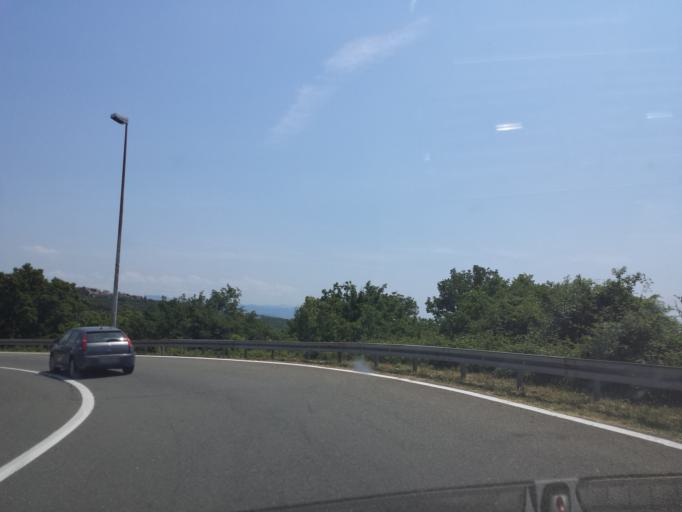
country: HR
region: Primorsko-Goranska
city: Matulji
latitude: 45.3600
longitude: 14.3247
